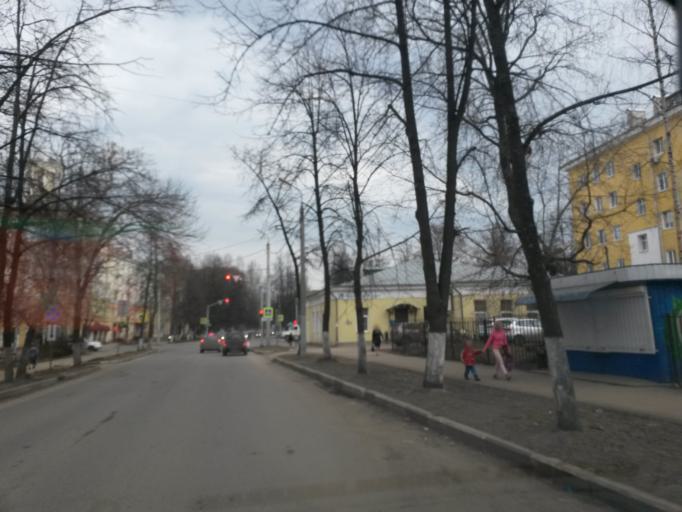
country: RU
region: Jaroslavl
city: Yaroslavl
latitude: 57.6257
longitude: 39.8624
